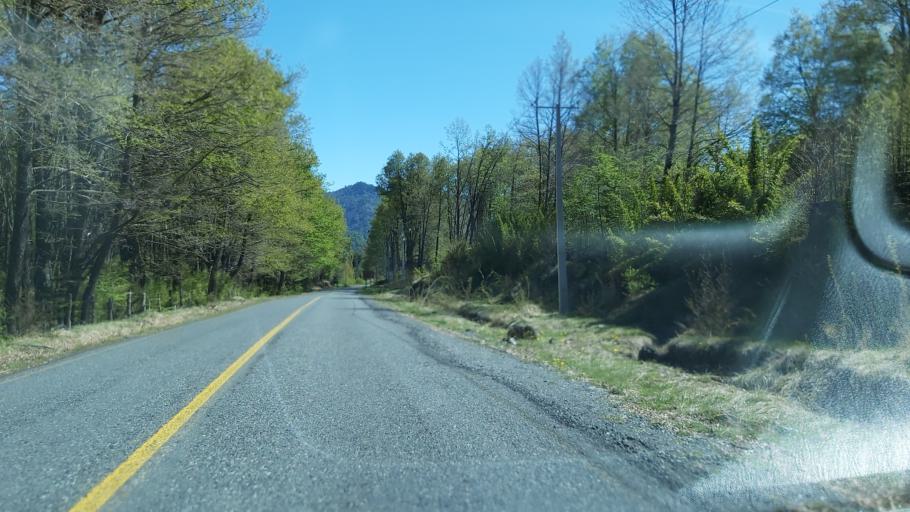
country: CL
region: Araucania
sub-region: Provincia de Cautin
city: Vilcun
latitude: -38.4661
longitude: -71.5196
